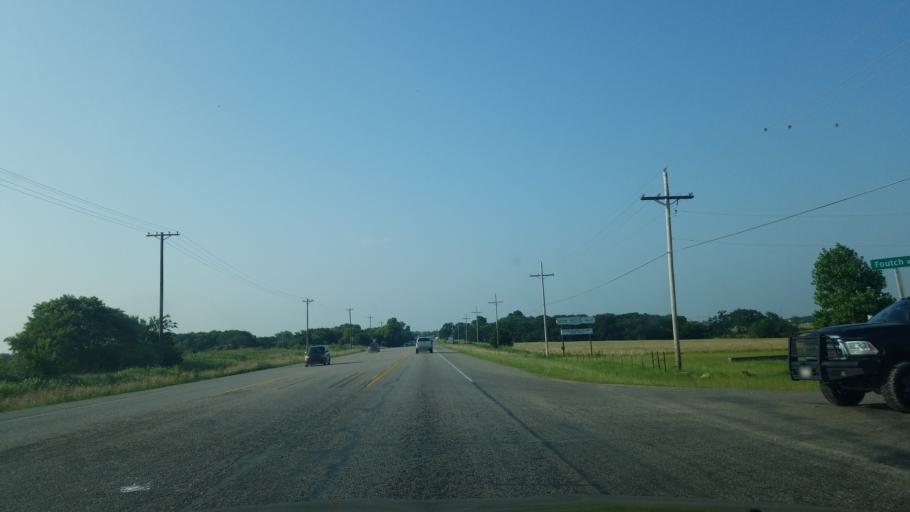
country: US
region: Texas
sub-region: Denton County
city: Pilot Point
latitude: 33.3712
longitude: -96.9638
